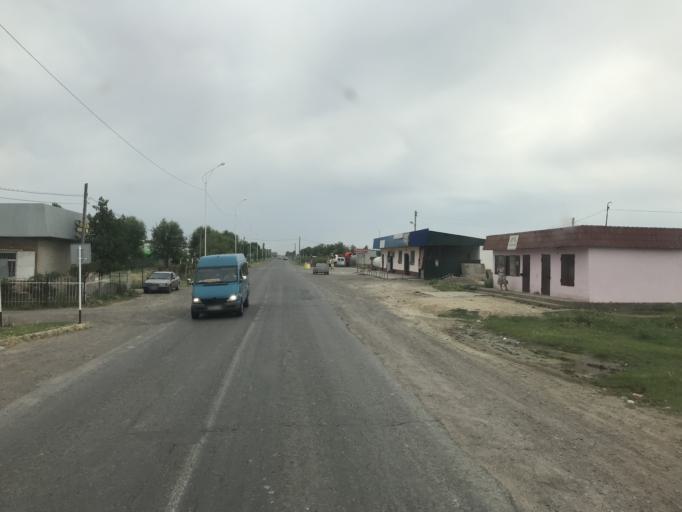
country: KZ
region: Ongtustik Qazaqstan
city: Asykata
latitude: 40.9342
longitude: 68.4095
